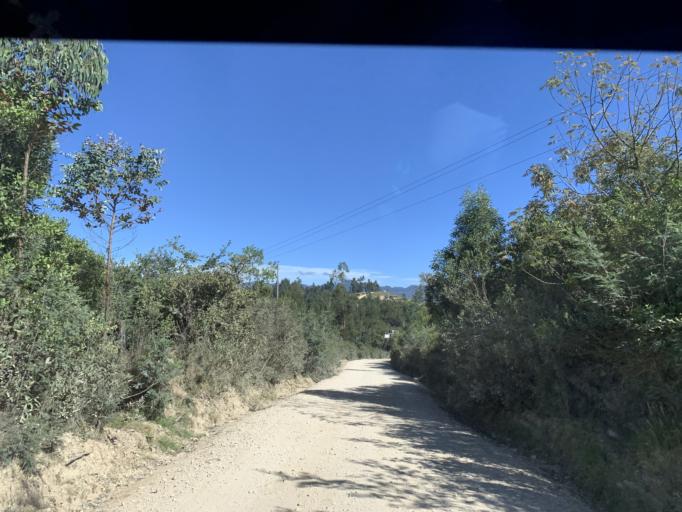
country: CO
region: Boyaca
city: Tuta
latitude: 5.7068
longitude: -73.1523
